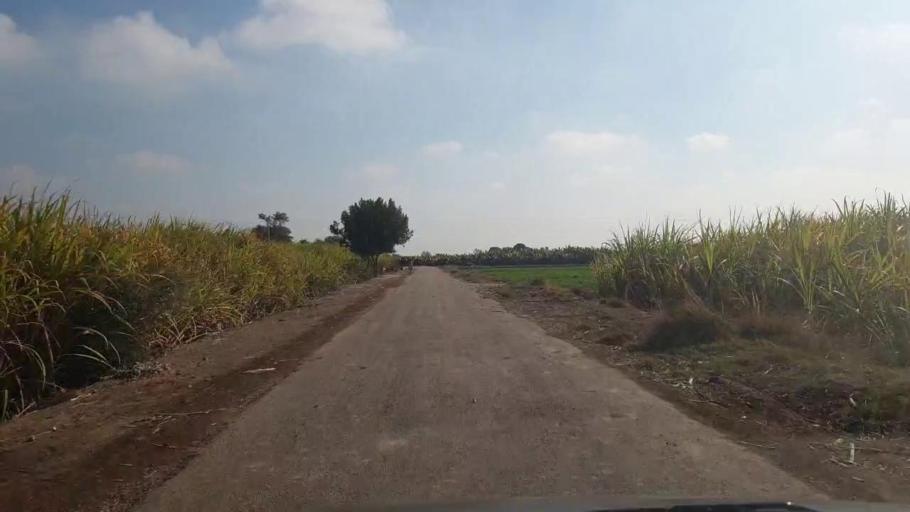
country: PK
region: Sindh
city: Shahdadpur
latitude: 25.8923
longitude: 68.5950
